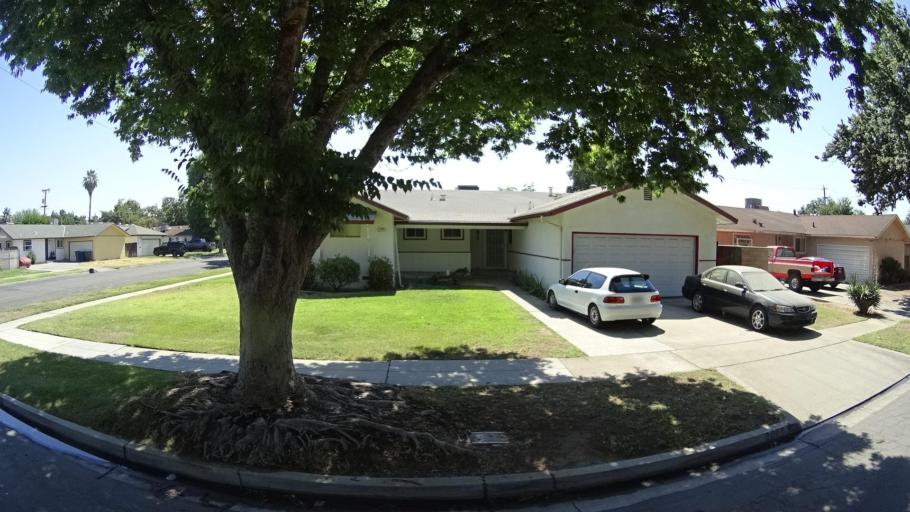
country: US
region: California
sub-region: Fresno County
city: Fresno
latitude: 36.7989
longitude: -119.7746
